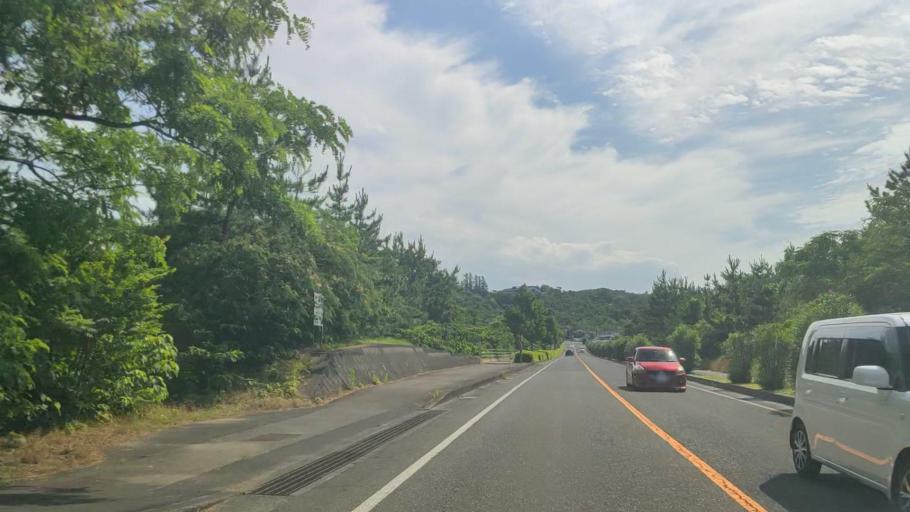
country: JP
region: Tottori
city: Tottori
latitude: 35.5360
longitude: 134.2337
